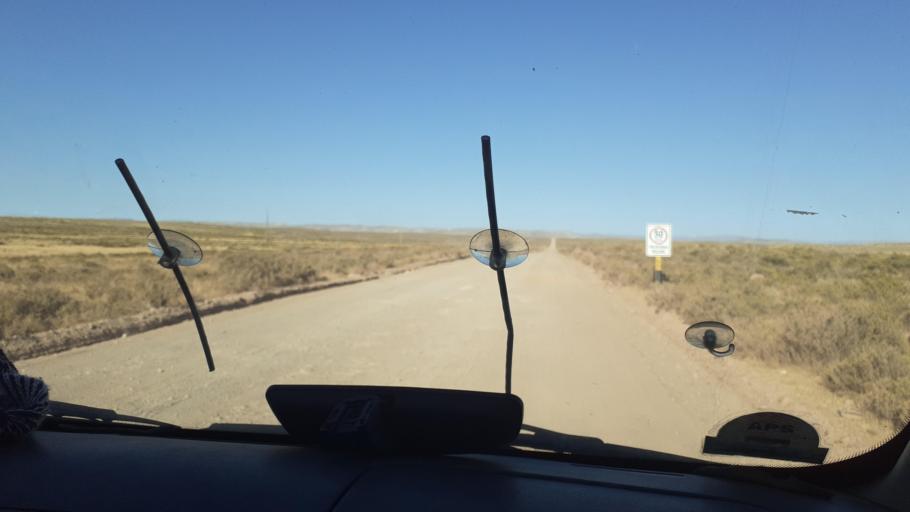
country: BO
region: La Paz
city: Tiahuanaco
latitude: -17.0929
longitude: -68.7562
